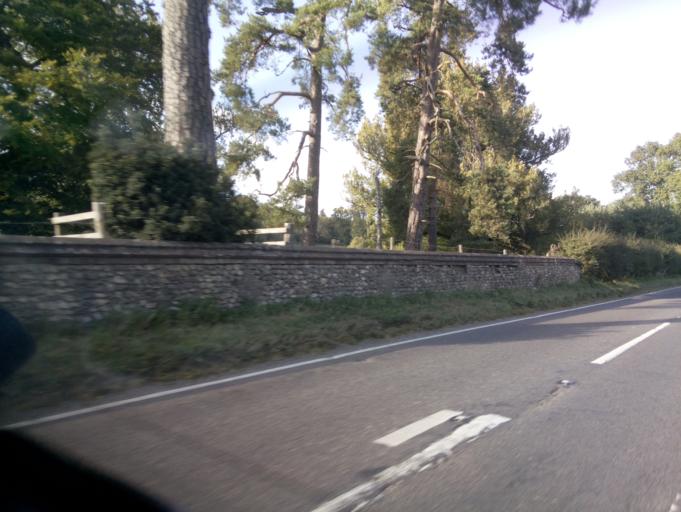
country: GB
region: England
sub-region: Hampshire
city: Four Marks
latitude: 51.0869
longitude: -1.0010
